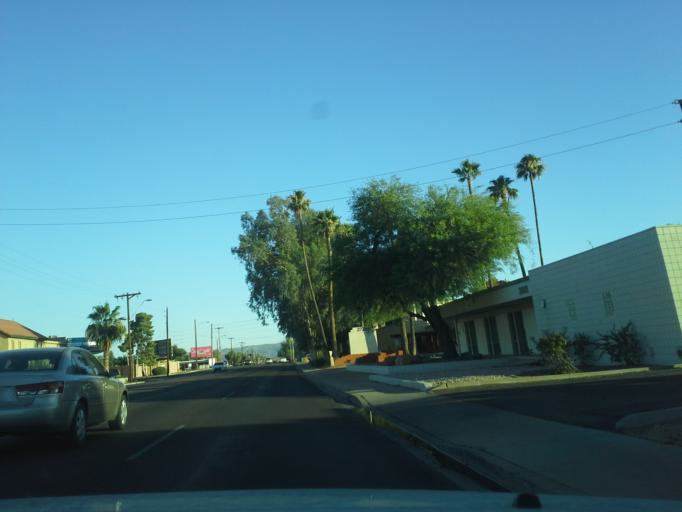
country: US
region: Arizona
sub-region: Maricopa County
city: Phoenix
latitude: 33.4787
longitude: -112.0303
